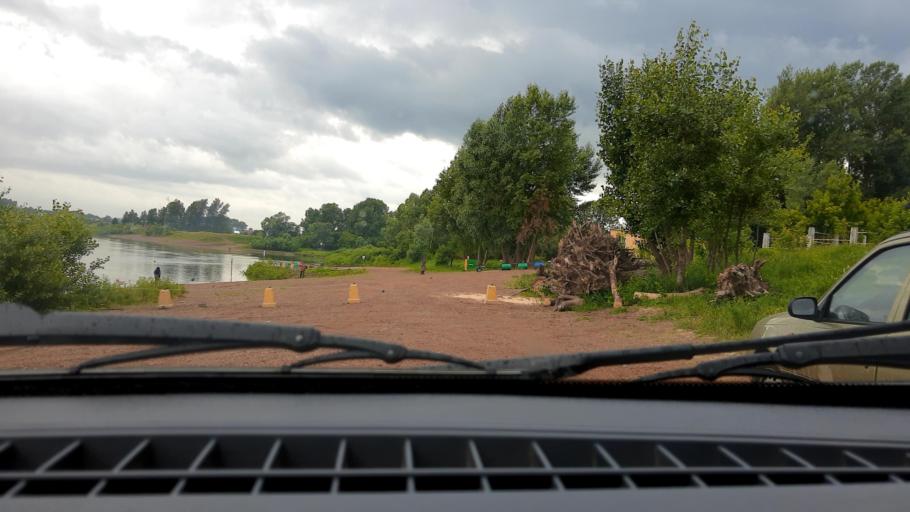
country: RU
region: Bashkortostan
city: Mikhaylovka
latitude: 54.7569
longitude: 55.9039
